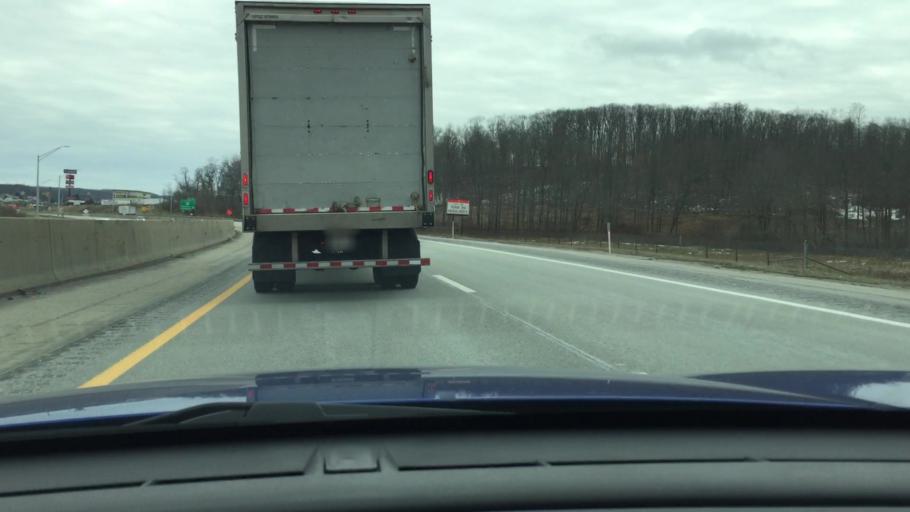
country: US
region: Pennsylvania
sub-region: Somerset County
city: Somerset
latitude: 40.0247
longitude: -79.0894
